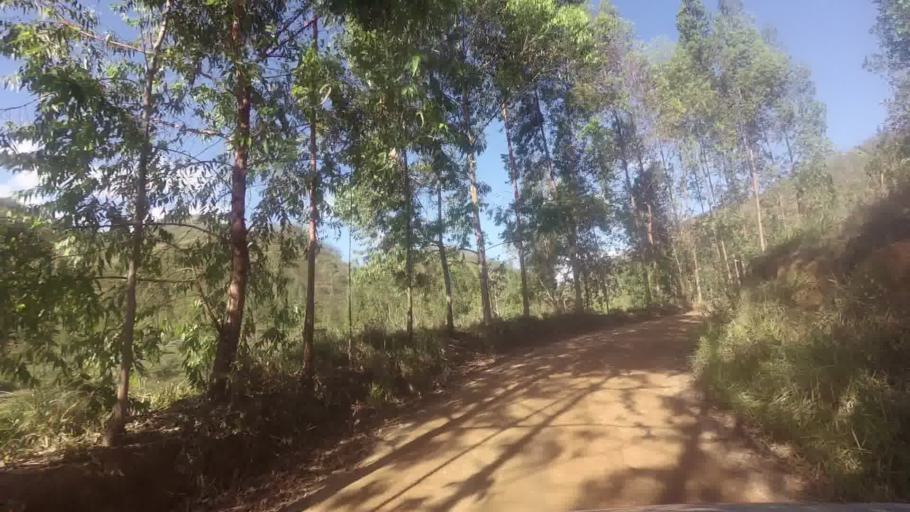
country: BR
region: Espirito Santo
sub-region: Sao Jose Do Calcado
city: Sao Jose do Calcado
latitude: -21.0255
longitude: -41.5778
